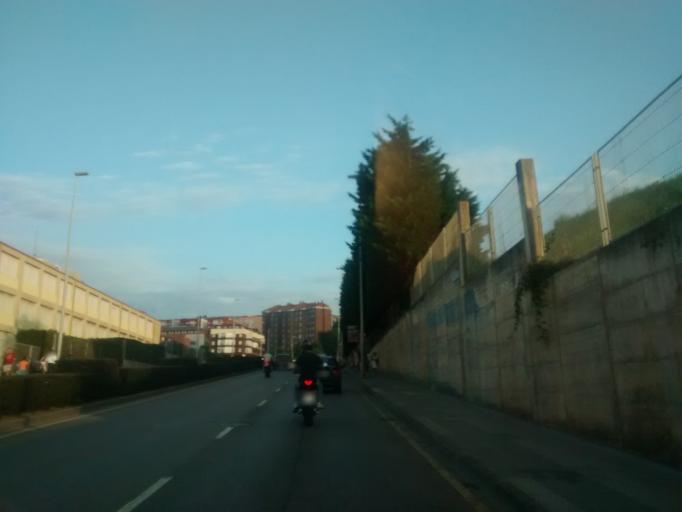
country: ES
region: Cantabria
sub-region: Provincia de Cantabria
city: Santander
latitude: 43.4741
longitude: -3.7940
